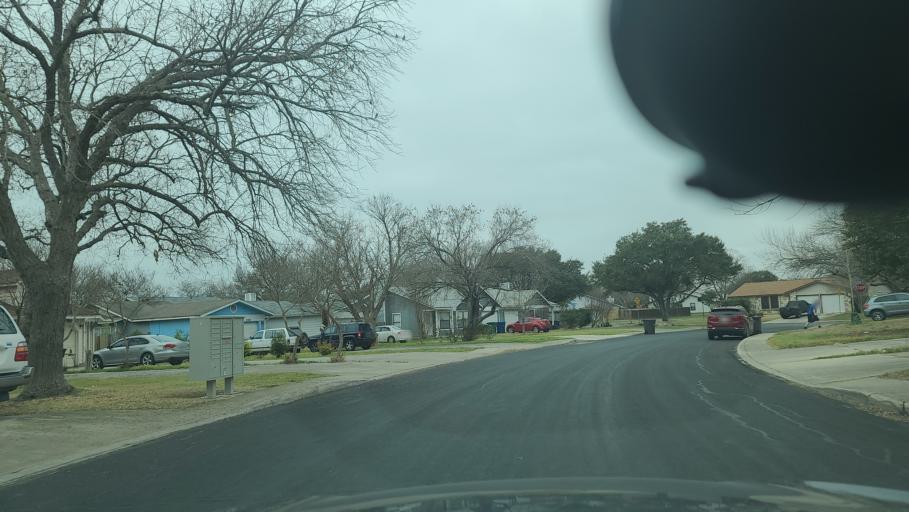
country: US
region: Texas
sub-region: Bexar County
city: Leon Valley
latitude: 29.5533
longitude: -98.6247
